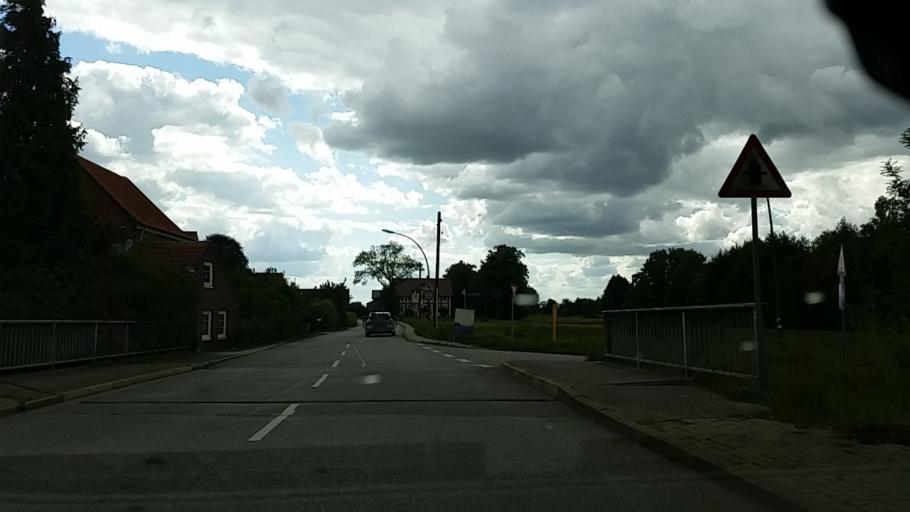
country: DE
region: Schleswig-Holstein
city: Bornsen
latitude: 53.4680
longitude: 10.2591
